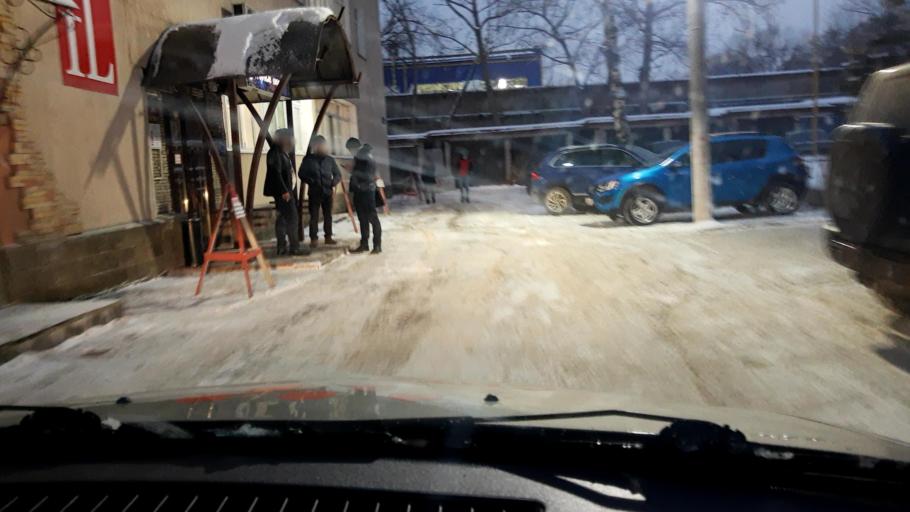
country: RU
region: Bashkortostan
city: Ufa
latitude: 54.8037
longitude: 56.1099
